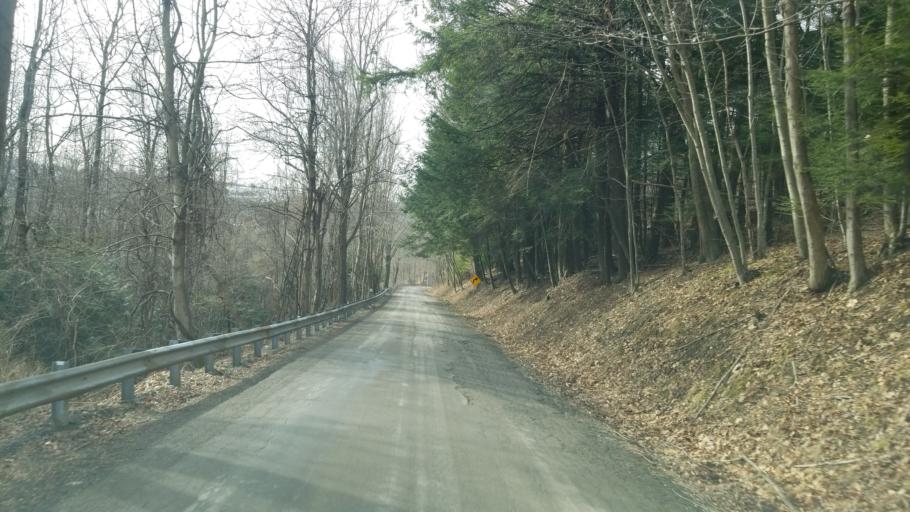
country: US
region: Pennsylvania
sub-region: Indiana County
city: Johnsonburg
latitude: 40.8344
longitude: -78.9014
